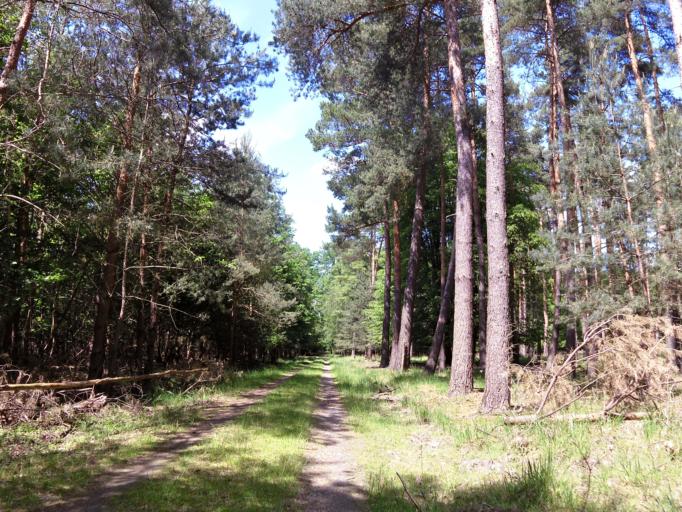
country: DE
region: Hesse
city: Kelsterbach
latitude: 50.0115
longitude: 8.5339
